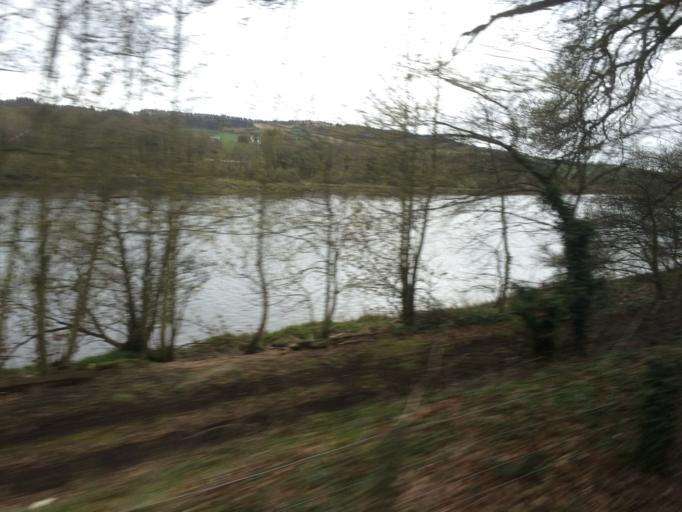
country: GB
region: Scotland
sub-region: Perth and Kinross
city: Scone
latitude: 56.3856
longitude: -3.3843
